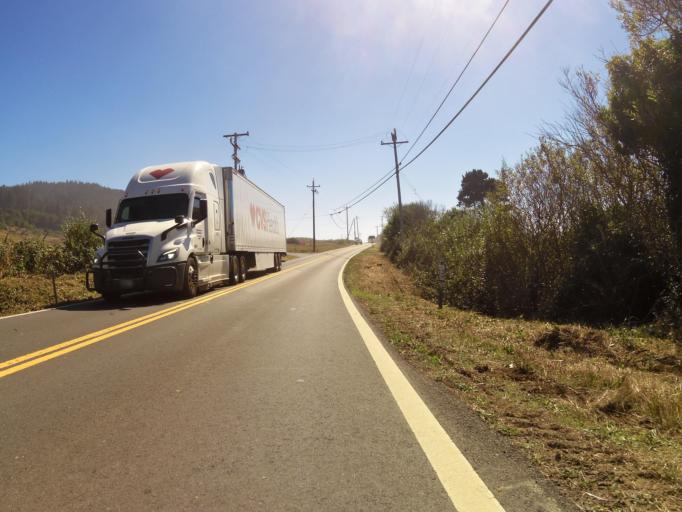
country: US
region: California
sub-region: Mendocino County
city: Fort Bragg
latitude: 39.6426
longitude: -123.7843
